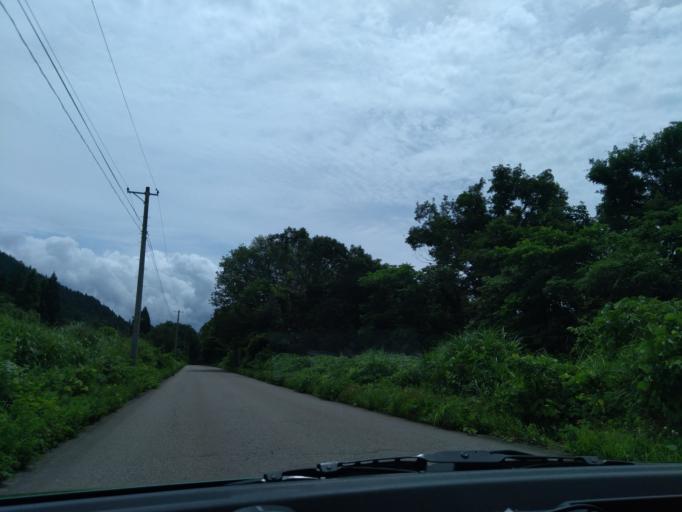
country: JP
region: Akita
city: Kakunodatemachi
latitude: 39.5751
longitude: 140.6296
